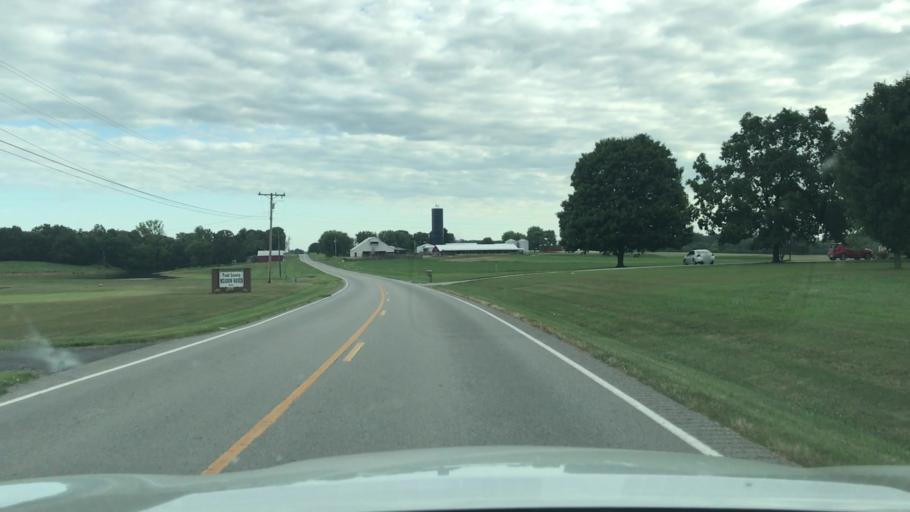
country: US
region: Kentucky
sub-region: Todd County
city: Elkton
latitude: 36.7563
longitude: -87.1677
